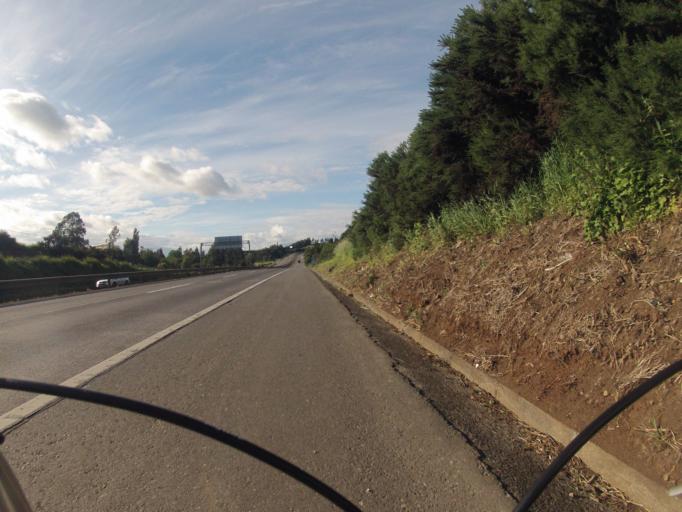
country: CL
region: Araucania
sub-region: Provincia de Cautin
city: Temuco
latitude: -38.8125
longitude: -72.6252
